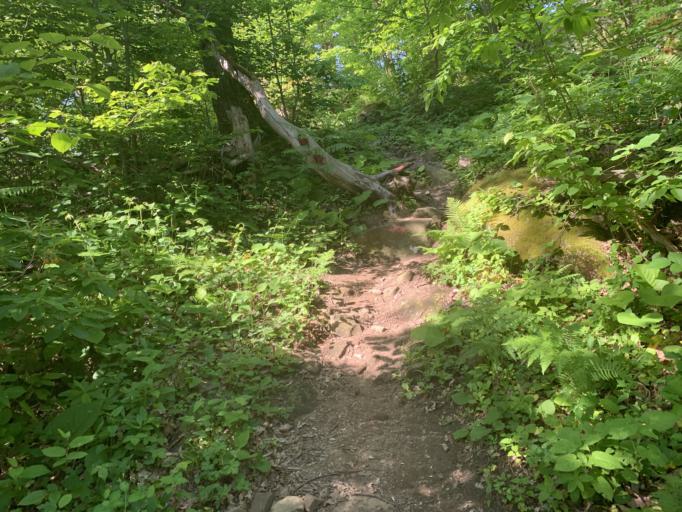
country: RU
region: Krasnodarskiy
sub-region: Sochi City
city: Lazarevskoye
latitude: 43.9519
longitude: 39.3258
